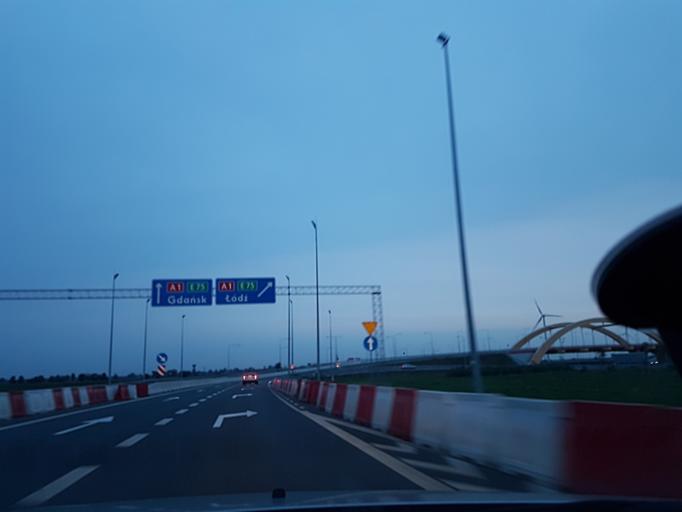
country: PL
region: Lodz Voivodeship
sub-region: Powiat kutnowski
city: Krzyzanow
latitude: 52.2227
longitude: 19.4655
